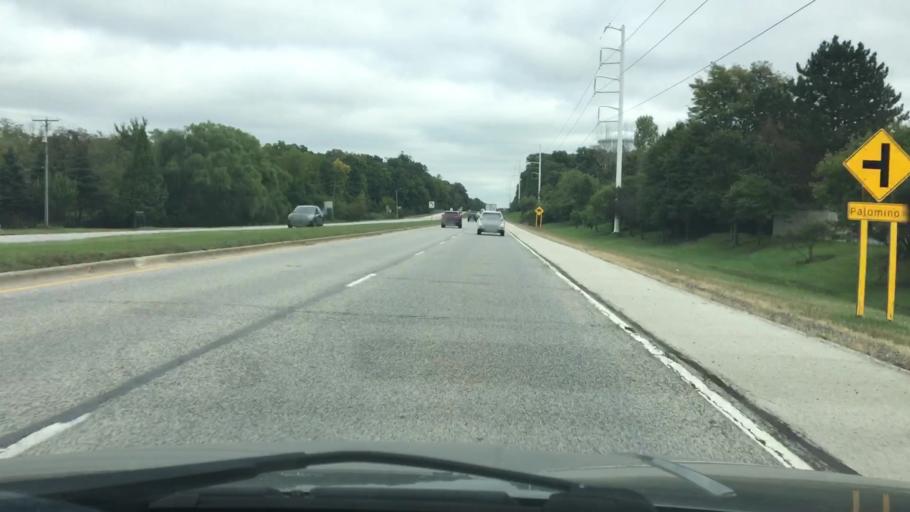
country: US
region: Illinois
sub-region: DuPage County
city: Woodridge
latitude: 41.7492
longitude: -88.0916
